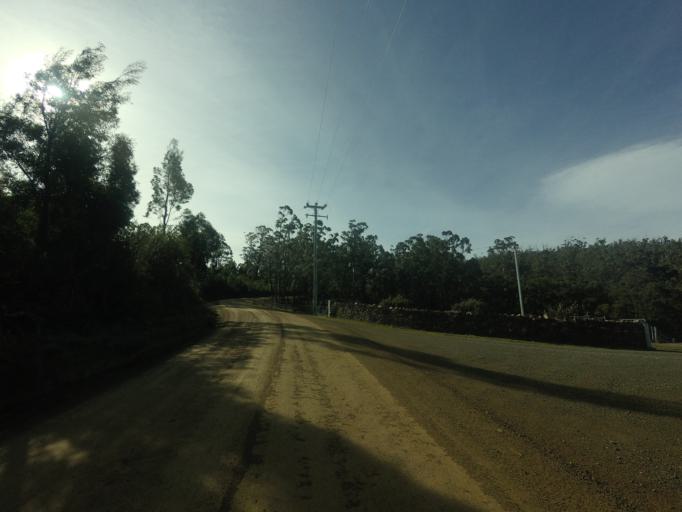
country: AU
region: Tasmania
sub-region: Kingborough
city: Kettering
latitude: -43.0927
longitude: 147.2648
